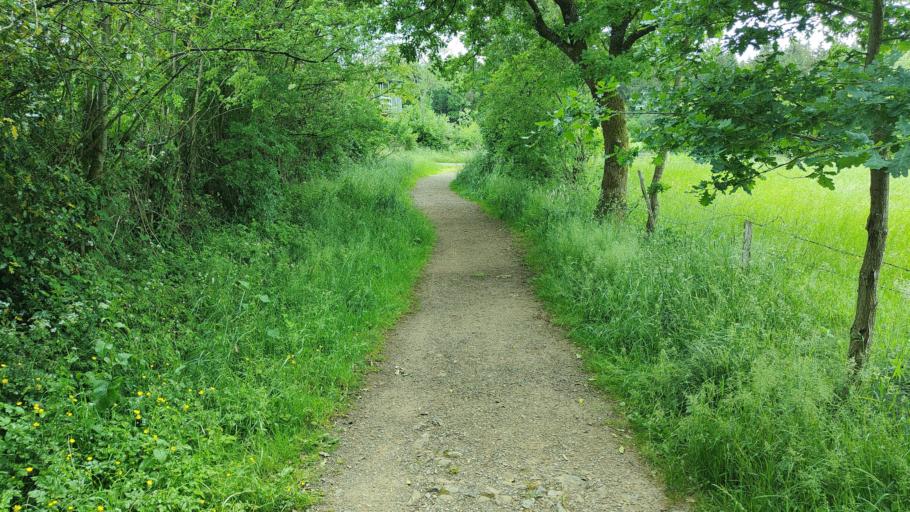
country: DE
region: North Rhine-Westphalia
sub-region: Regierungsbezirk Koln
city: Roetgen
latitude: 50.6356
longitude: 6.1803
